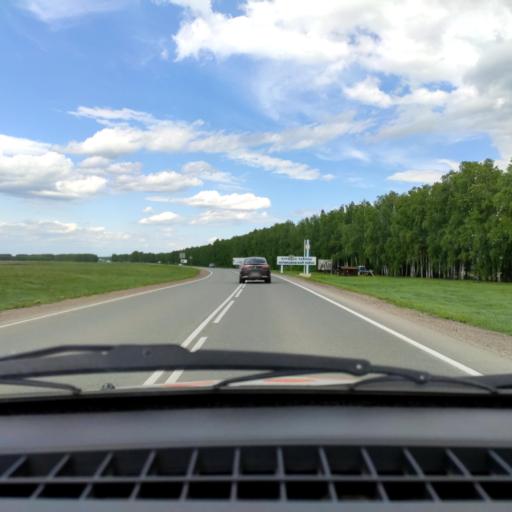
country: RU
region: Bashkortostan
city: Iglino
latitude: 54.9702
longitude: 56.4987
